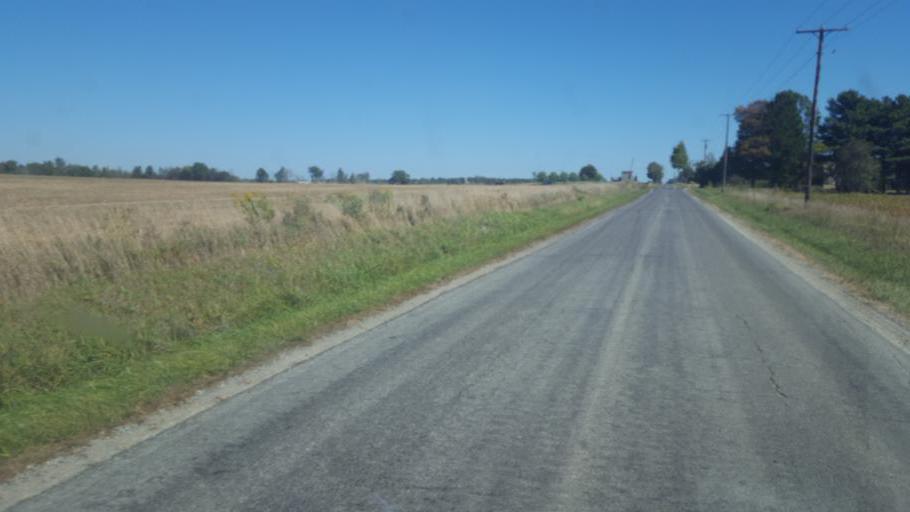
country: US
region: Ohio
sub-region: Huron County
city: Greenwich
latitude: 40.9930
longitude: -82.4976
